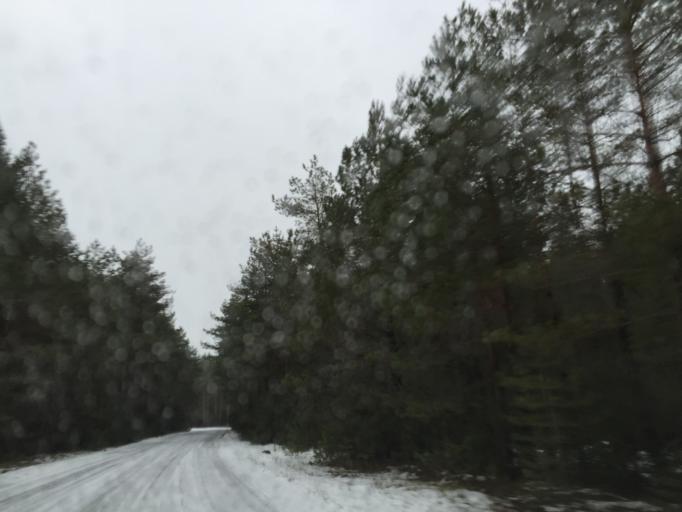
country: EE
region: Laeaene
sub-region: Lihula vald
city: Lihula
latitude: 58.6158
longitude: 23.5568
